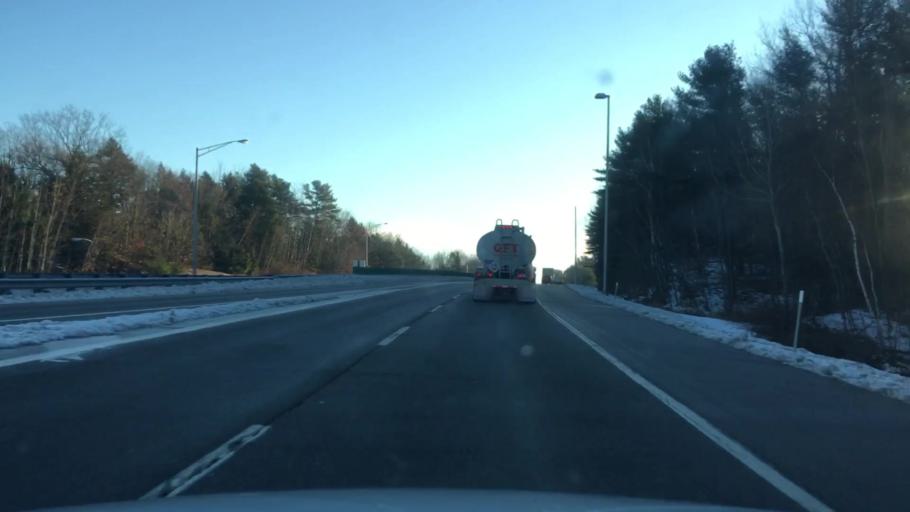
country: US
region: Maine
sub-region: Sagadahoc County
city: Topsham
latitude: 43.9169
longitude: -70.0167
